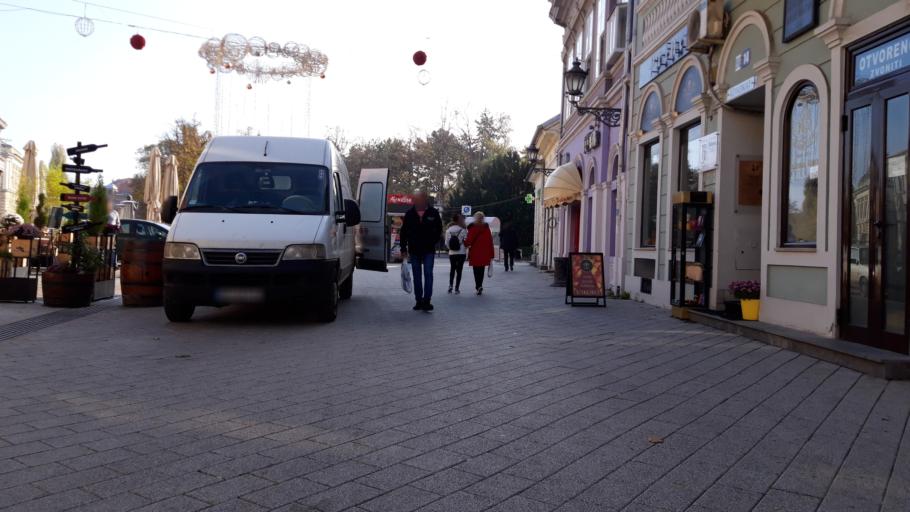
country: RS
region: Autonomna Pokrajina Vojvodina
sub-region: Juznobacki Okrug
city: Novi Sad
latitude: 45.2564
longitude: 19.8495
